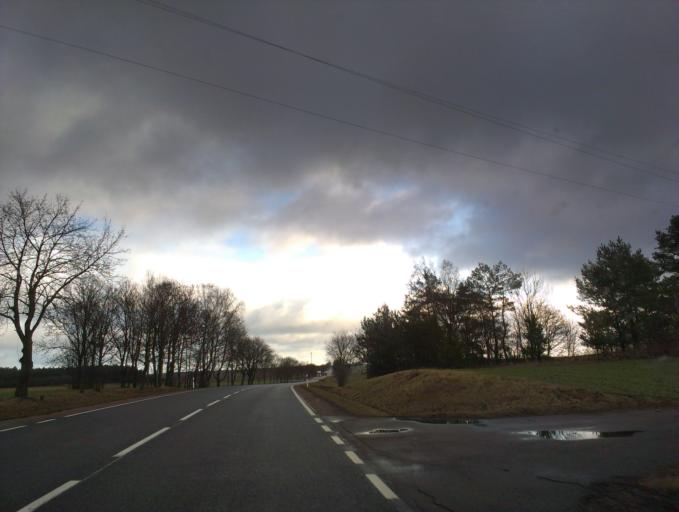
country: PL
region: Pomeranian Voivodeship
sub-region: Powiat czluchowski
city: Debrzno
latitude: 53.6313
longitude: 17.2571
